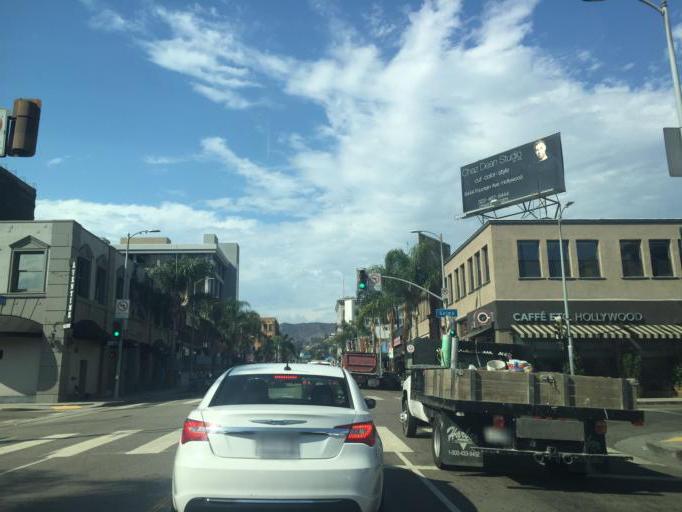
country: US
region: California
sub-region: Los Angeles County
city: Hollywood
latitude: 34.0996
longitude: -118.3295
